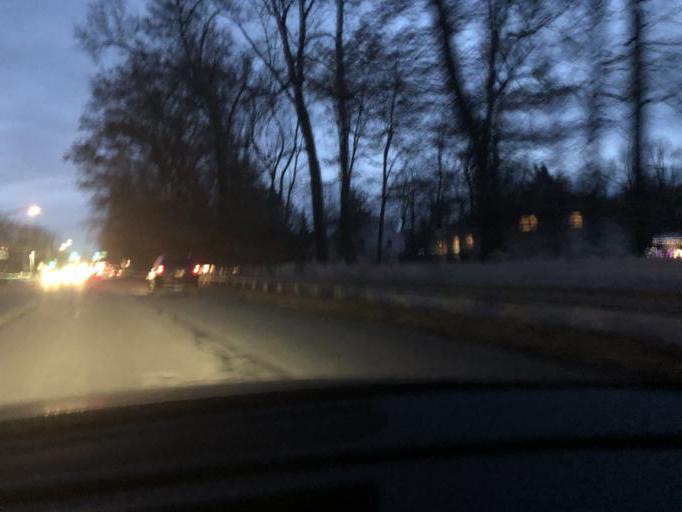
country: US
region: New Jersey
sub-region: Morris County
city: Florham Park
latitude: 40.7841
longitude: -74.3813
